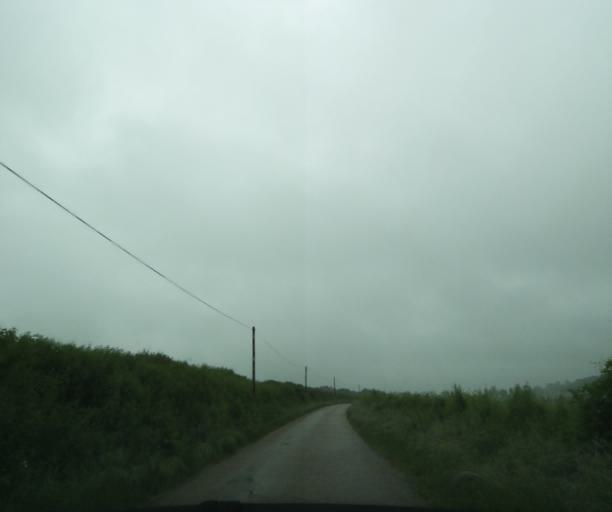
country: FR
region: Bourgogne
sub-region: Departement de Saone-et-Loire
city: Charolles
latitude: 46.3961
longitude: 4.2913
